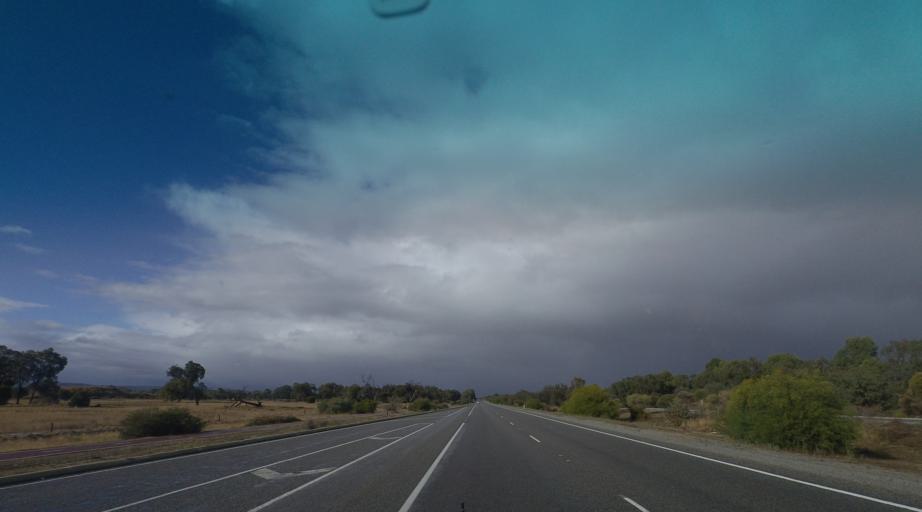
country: AU
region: Western Australia
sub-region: Serpentine-Jarrahdale
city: Oakford
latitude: -32.1866
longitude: 115.9625
